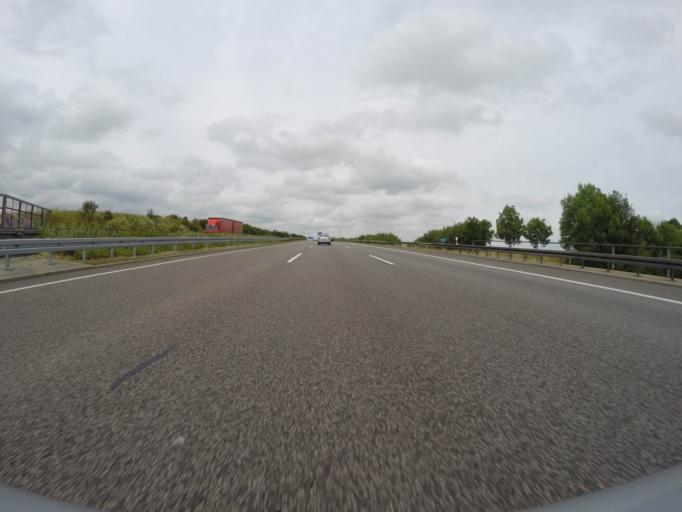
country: DE
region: Thuringia
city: Vollersroda
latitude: 50.9433
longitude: 11.3162
